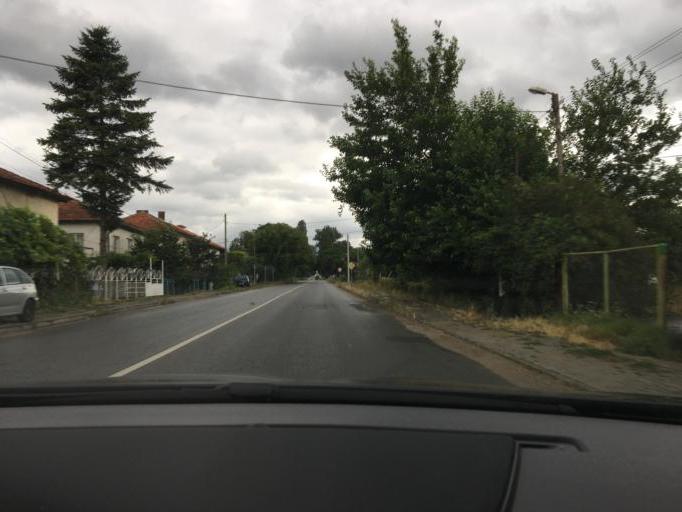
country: BG
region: Kyustendil
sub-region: Obshtina Kyustendil
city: Kyustendil
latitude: 42.2798
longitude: 22.7313
